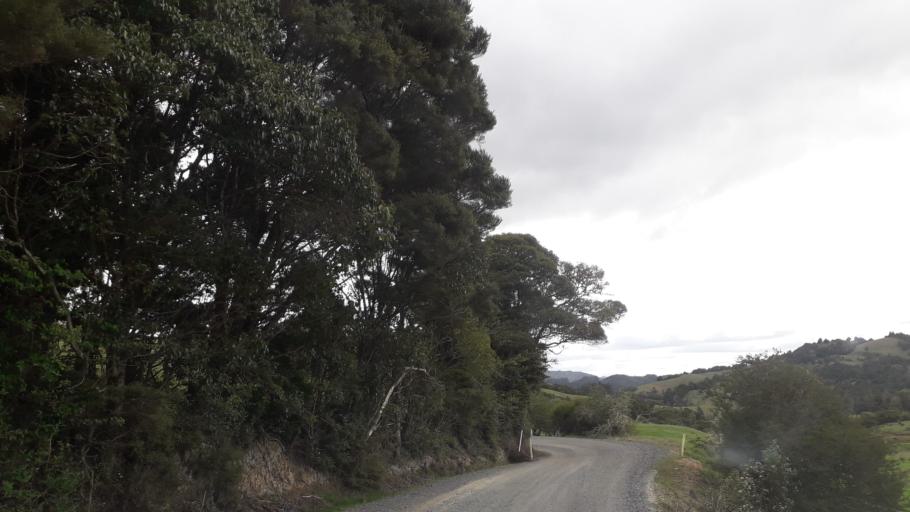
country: NZ
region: Northland
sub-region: Far North District
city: Kerikeri
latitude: -35.1312
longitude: 173.7288
